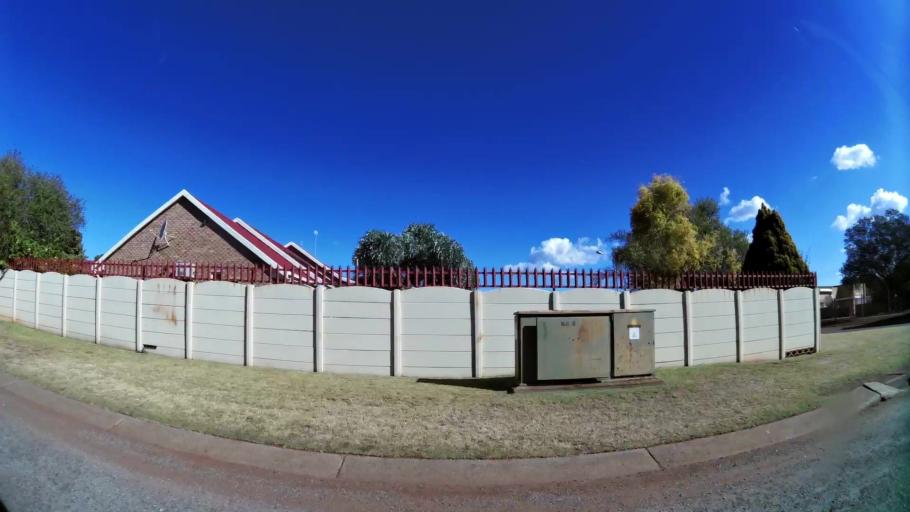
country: ZA
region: Gauteng
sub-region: West Rand District Municipality
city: Carletonville
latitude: -26.3592
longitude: 27.3711
